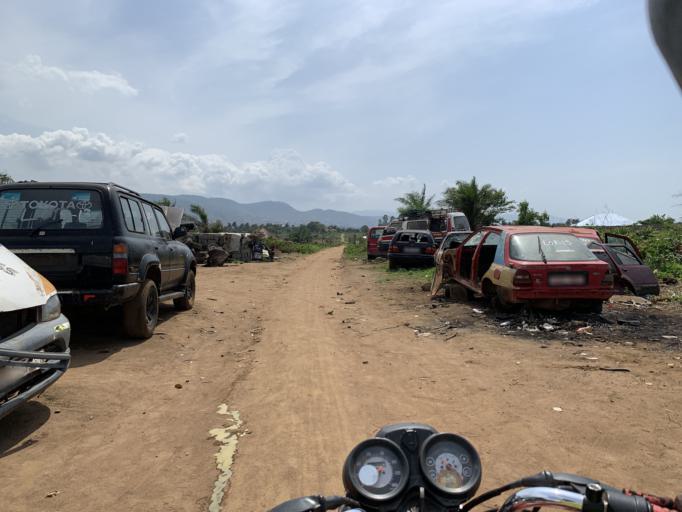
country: SL
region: Western Area
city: Waterloo
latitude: 8.3561
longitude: -13.0462
